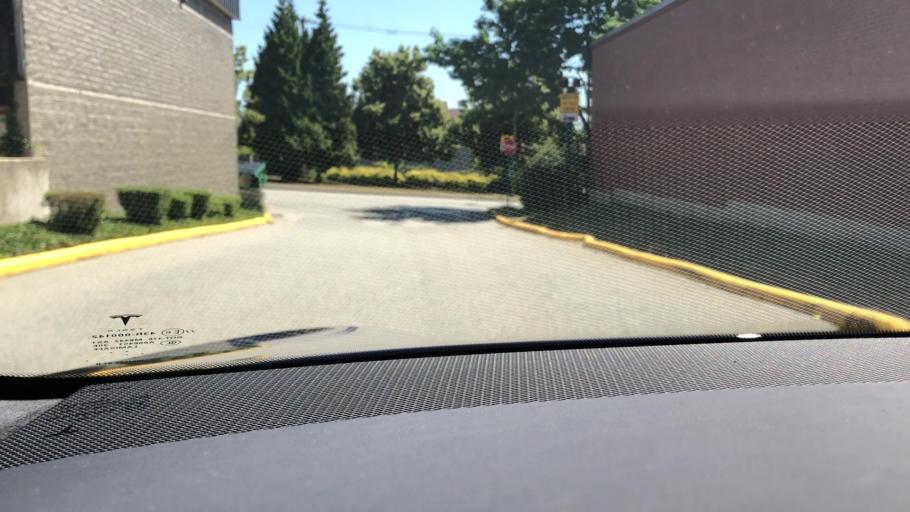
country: CA
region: British Columbia
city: Port Moody
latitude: 49.2483
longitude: -122.8661
